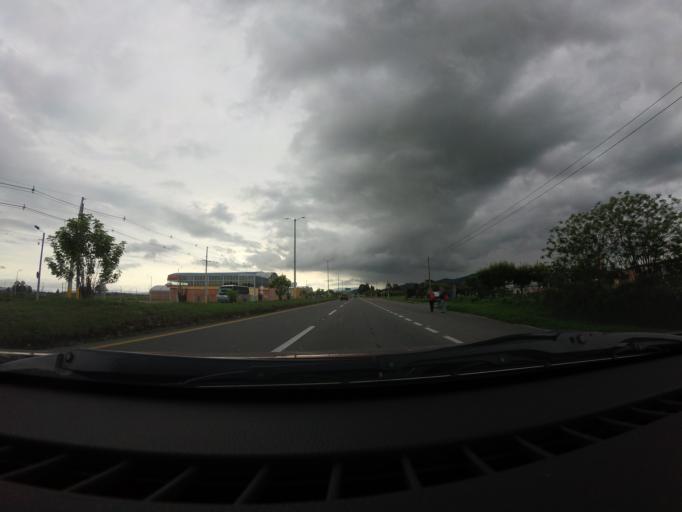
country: CO
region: Cundinamarca
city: Funza
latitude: 4.7836
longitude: -74.1890
